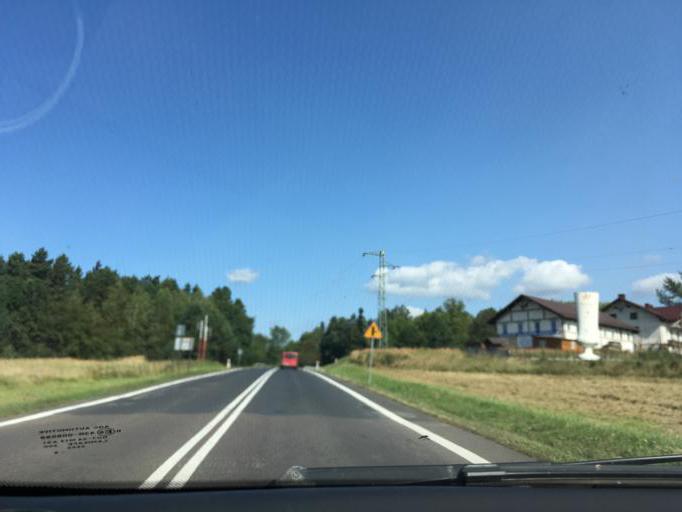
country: PL
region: Subcarpathian Voivodeship
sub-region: Powiat sanocki
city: Zagorz
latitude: 49.5012
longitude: 22.3002
